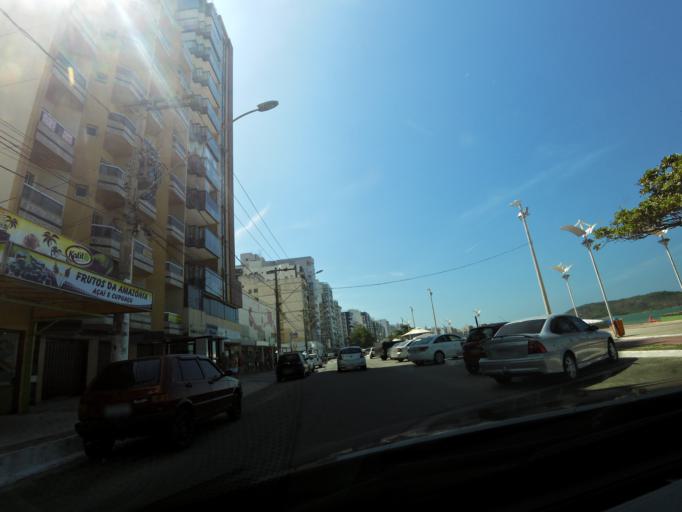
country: BR
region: Espirito Santo
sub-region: Guarapari
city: Guarapari
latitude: -20.6565
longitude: -40.4913
